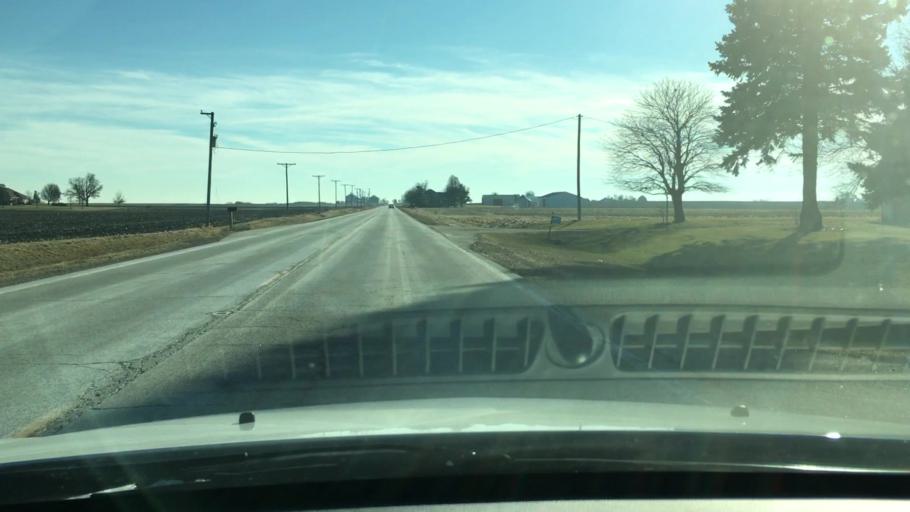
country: US
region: Illinois
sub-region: LaSalle County
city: Mendota
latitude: 41.6132
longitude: -89.1288
